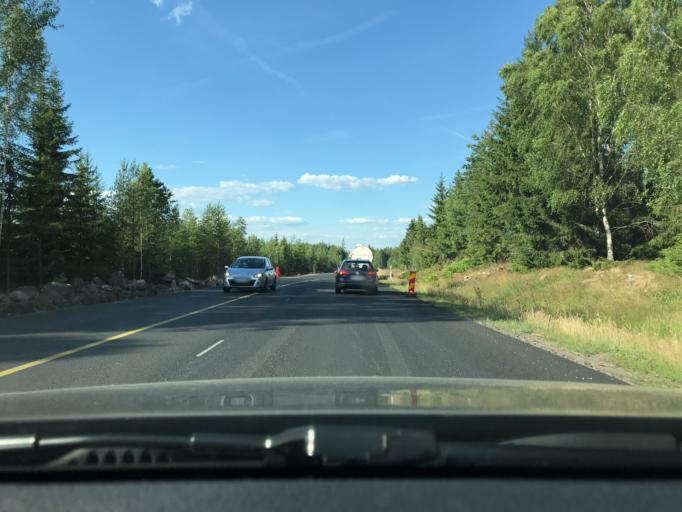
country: SE
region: Kronoberg
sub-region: Almhults Kommun
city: AElmhult
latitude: 56.5756
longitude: 14.1858
